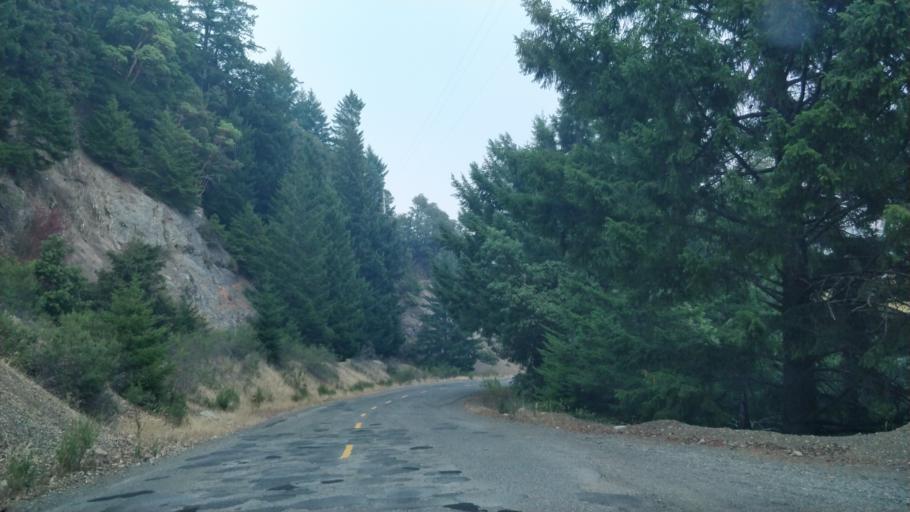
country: US
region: California
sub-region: Humboldt County
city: Rio Dell
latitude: 40.2727
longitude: -124.0791
